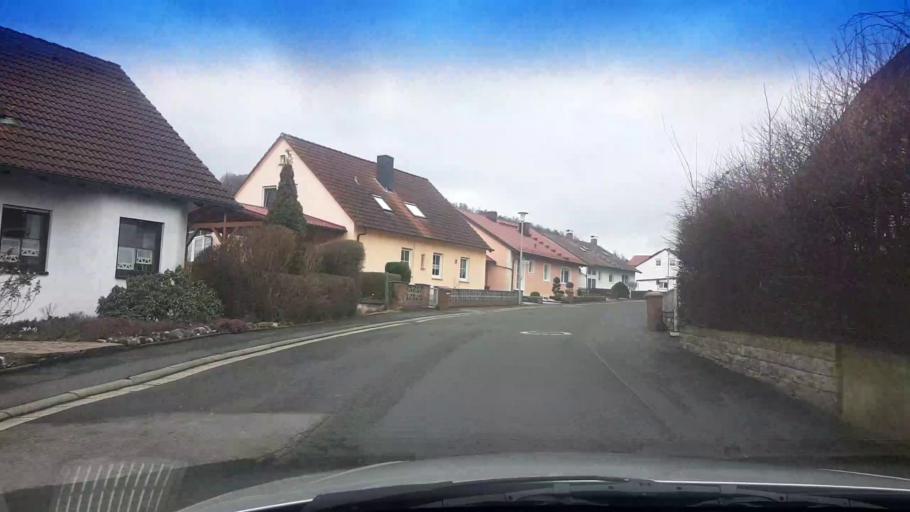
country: DE
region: Bavaria
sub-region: Regierungsbezirk Unterfranken
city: Sand
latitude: 49.9436
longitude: 10.6035
